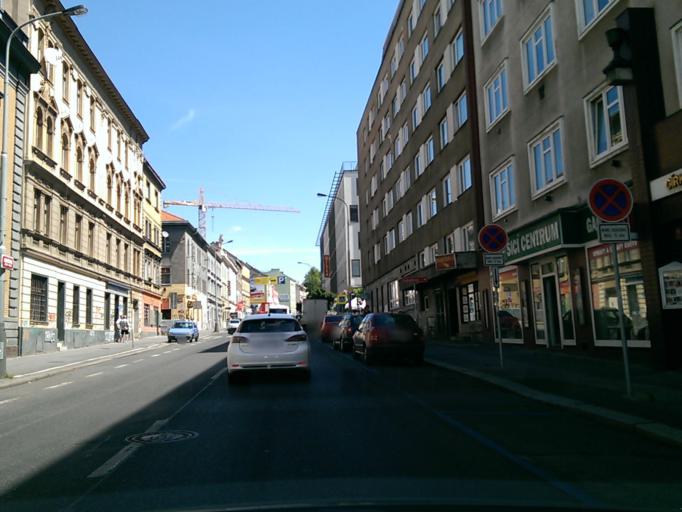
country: CZ
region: Praha
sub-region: Praha 8
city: Karlin
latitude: 50.0875
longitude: 14.4558
